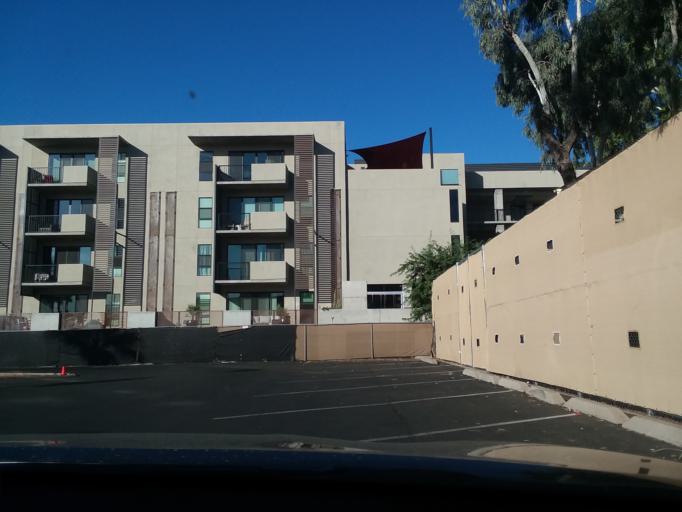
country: US
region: Arizona
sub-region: Maricopa County
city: Phoenix
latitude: 33.5027
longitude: -112.0321
